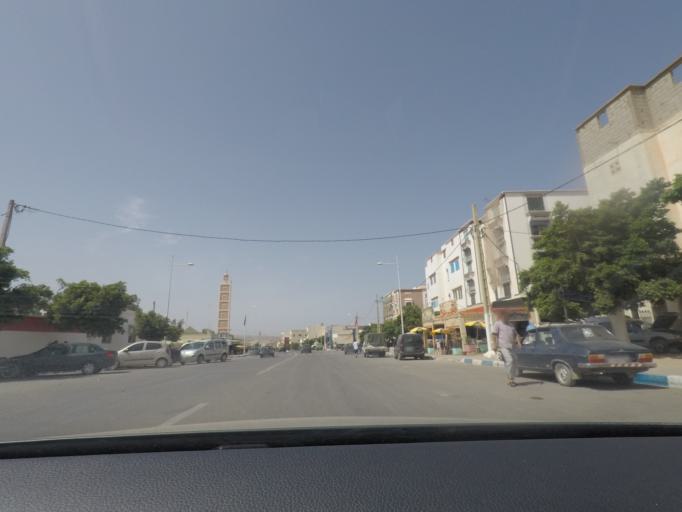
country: MA
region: Marrakech-Tensift-Al Haouz
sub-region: Essaouira
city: Tamanar
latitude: 31.0039
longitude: -9.6767
